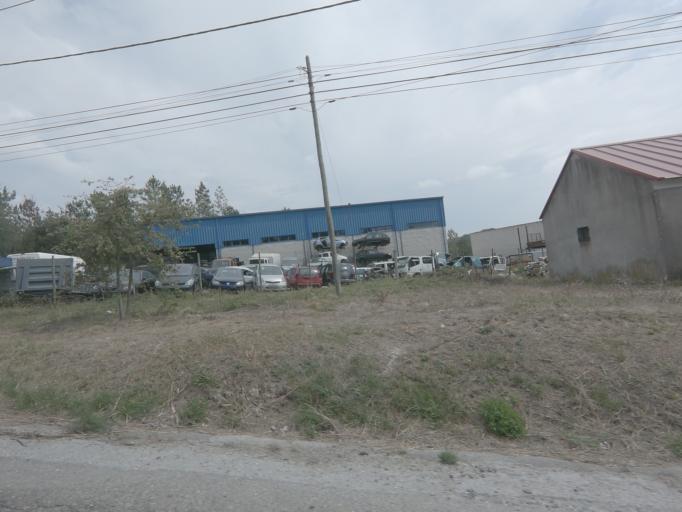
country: PT
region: Leiria
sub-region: Leiria
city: Caranguejeira
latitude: 39.8134
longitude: -8.7356
